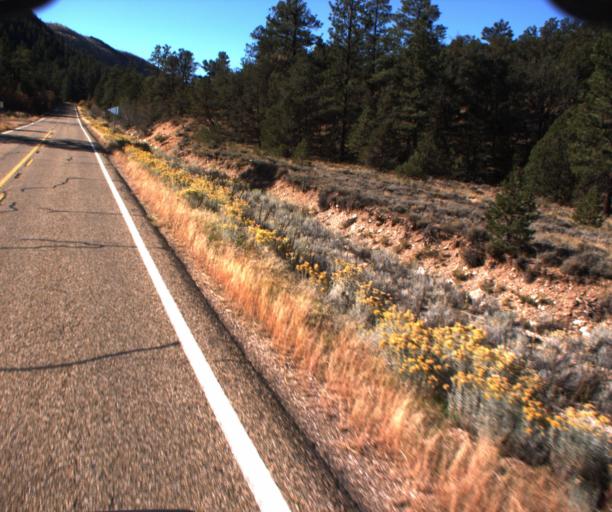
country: US
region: Arizona
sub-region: Coconino County
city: Fredonia
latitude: 36.7427
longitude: -112.1242
